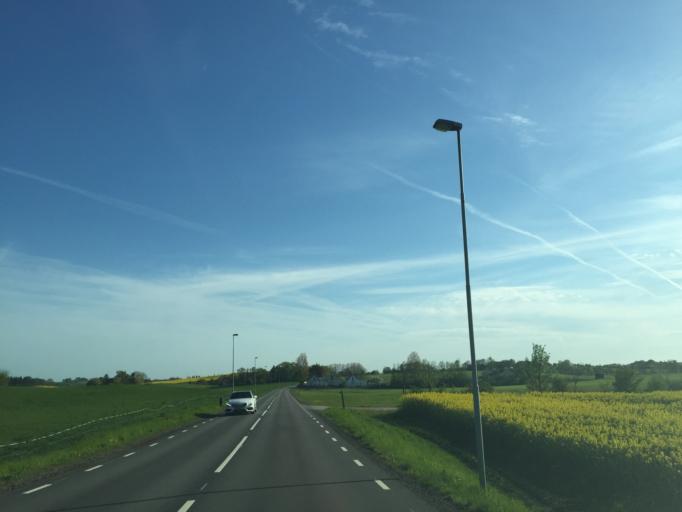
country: SE
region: Skane
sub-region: Malmo
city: Oxie
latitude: 55.5700
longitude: 13.1171
